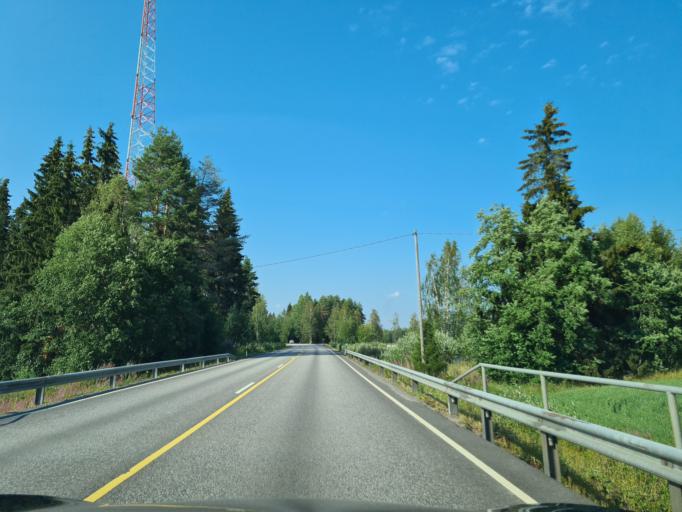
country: FI
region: Satakunta
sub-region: Pohjois-Satakunta
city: Kankaanpaeae
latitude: 61.9417
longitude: 22.5110
